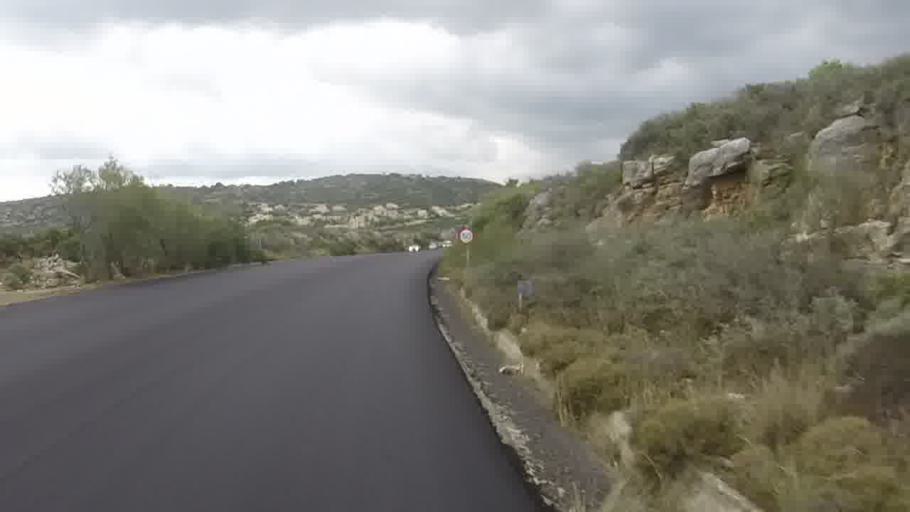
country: GR
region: Crete
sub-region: Nomos Rethymnis
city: Atsipopoulon
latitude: 35.3616
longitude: 24.4050
